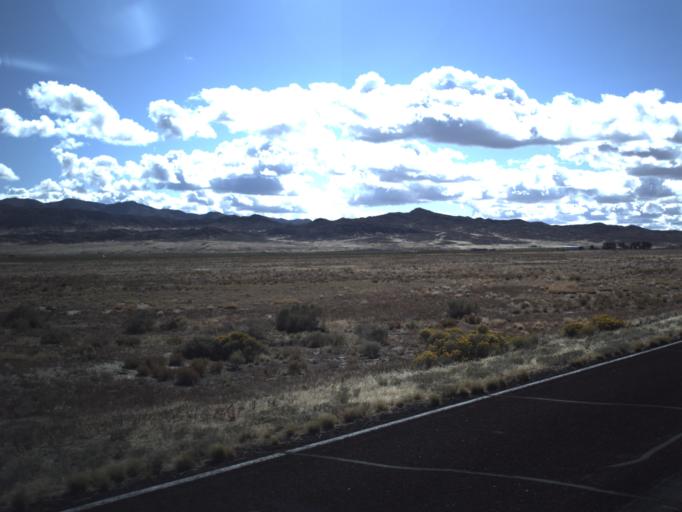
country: US
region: Nevada
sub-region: White Pine County
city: McGill
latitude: 38.9642
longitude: -114.0337
